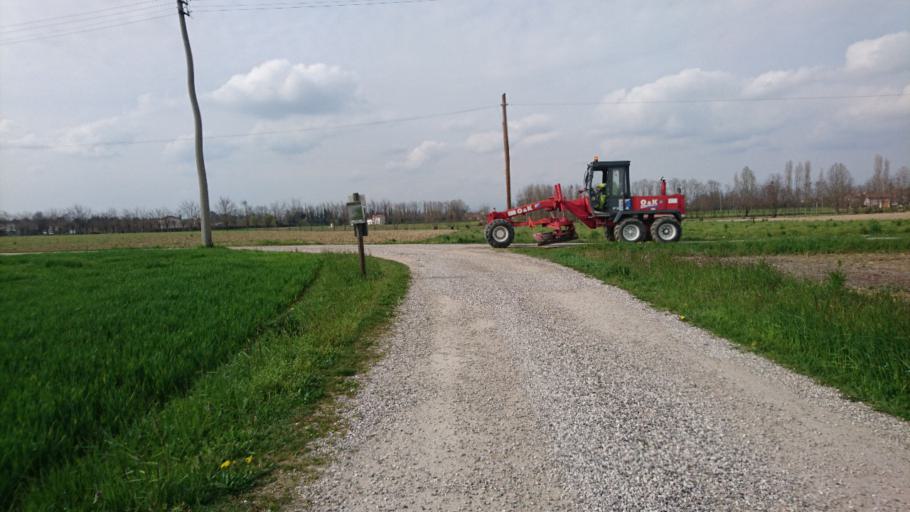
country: IT
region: Veneto
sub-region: Provincia di Padova
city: Tremignon
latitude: 45.5320
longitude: 11.8005
